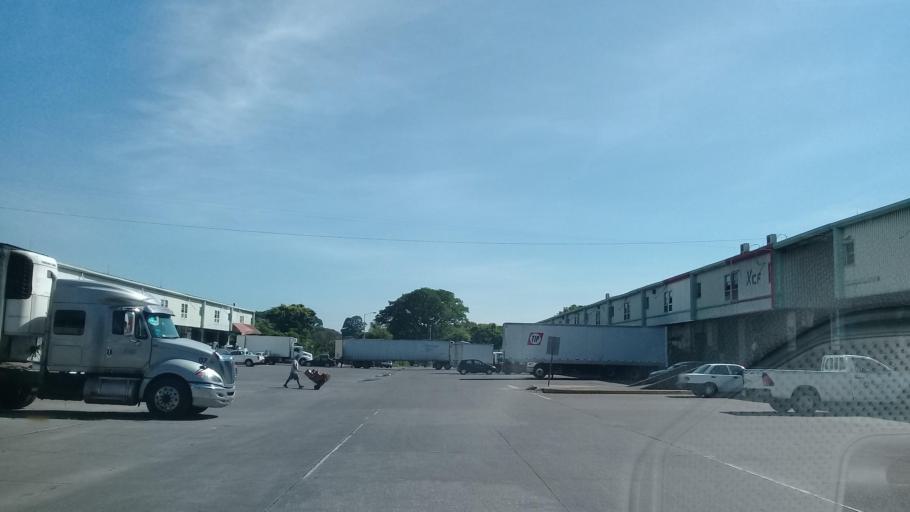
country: MX
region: Veracruz
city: Amatlan de los Reyes
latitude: 18.8576
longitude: -96.9117
